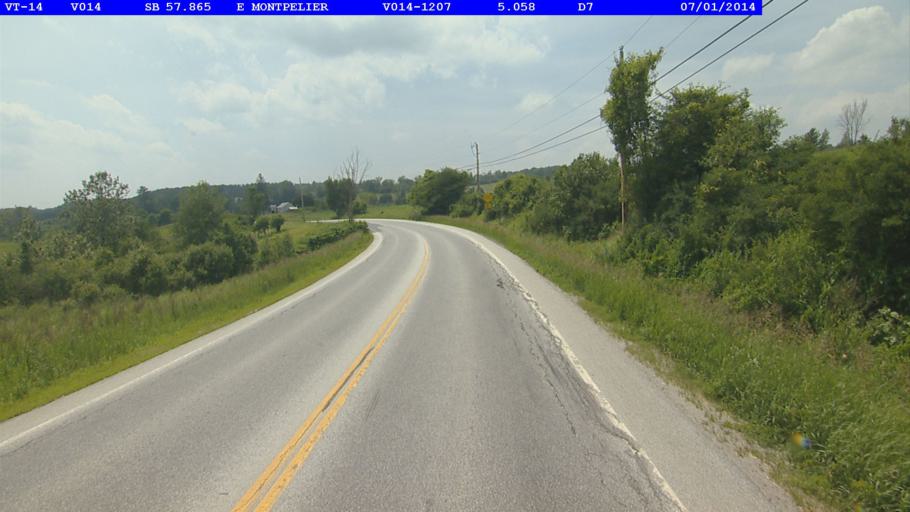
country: US
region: Vermont
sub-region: Washington County
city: Barre
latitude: 44.2986
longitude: -72.4526
